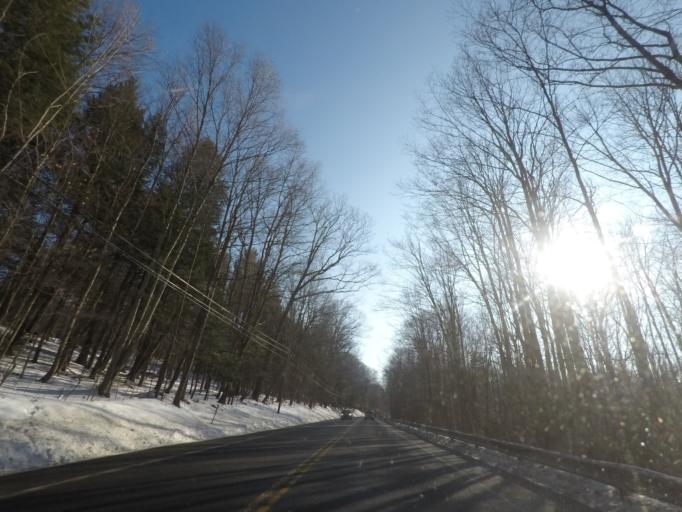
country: US
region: Massachusetts
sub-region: Berkshire County
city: Richmond
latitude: 42.5009
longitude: -73.3692
